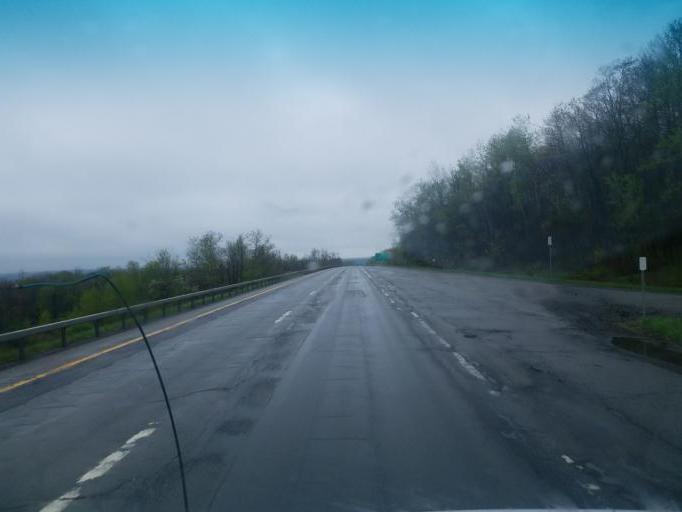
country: US
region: New York
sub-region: Chautauqua County
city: Lakewood
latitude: 42.1444
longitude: -79.3578
